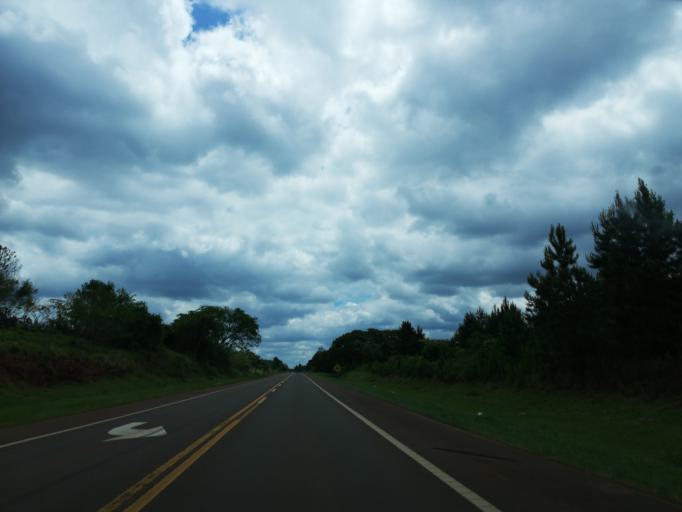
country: AR
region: Misiones
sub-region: Departamento de Leandro N. Alem
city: Leandro N. Alem
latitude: -27.6451
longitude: -55.3745
